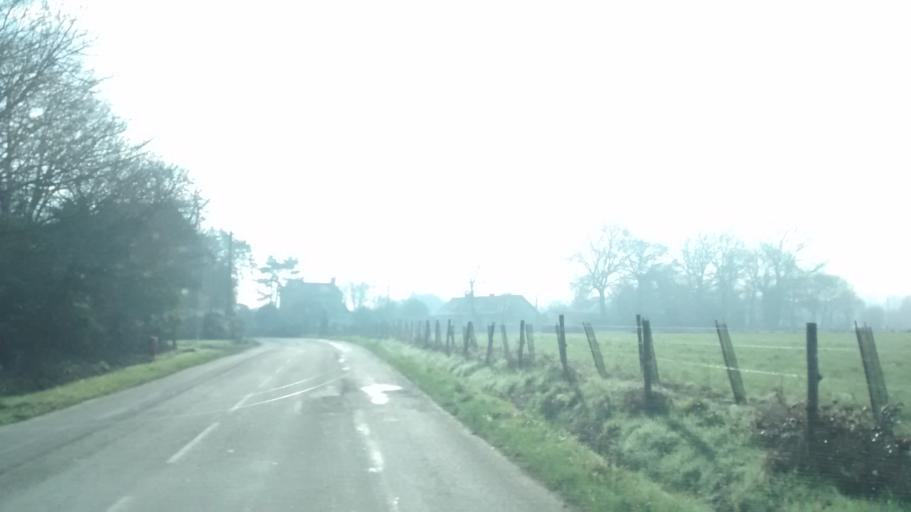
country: FR
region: Brittany
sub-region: Departement d'Ille-et-Vilaine
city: Betton
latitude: 48.1769
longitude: -1.6063
